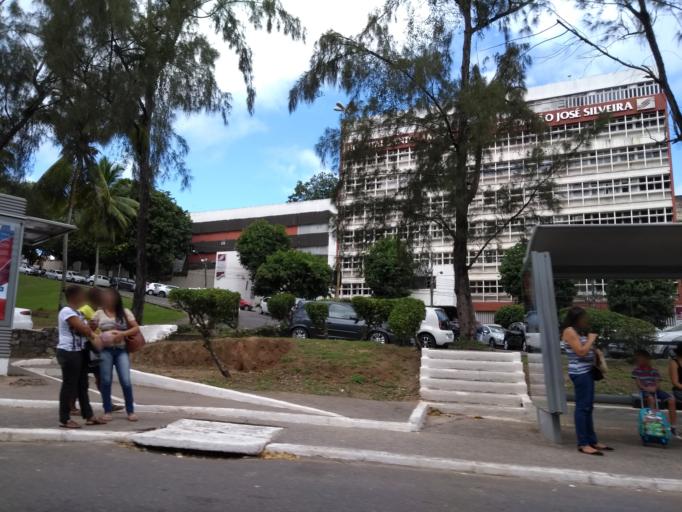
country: BR
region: Bahia
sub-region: Salvador
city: Salvador
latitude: -12.9977
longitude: -38.5167
